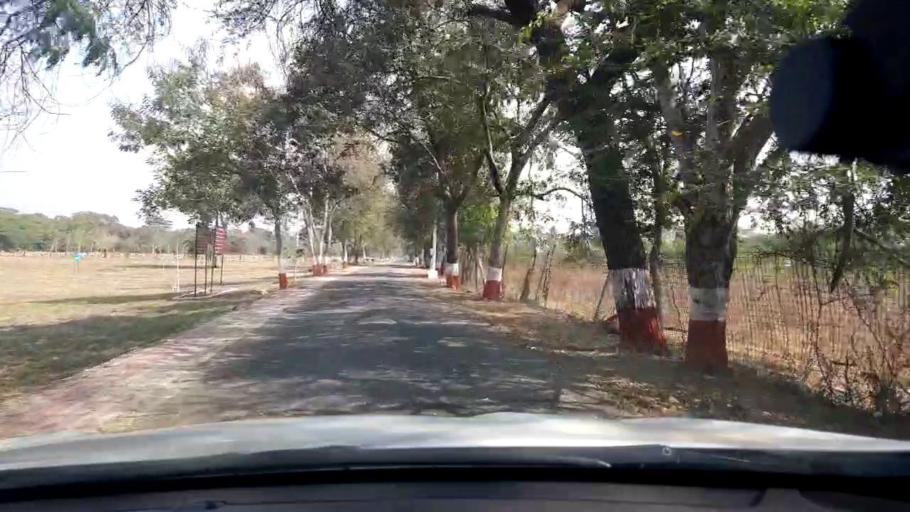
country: IN
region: Maharashtra
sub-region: Pune Division
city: Shivaji Nagar
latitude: 18.5406
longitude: 73.8590
